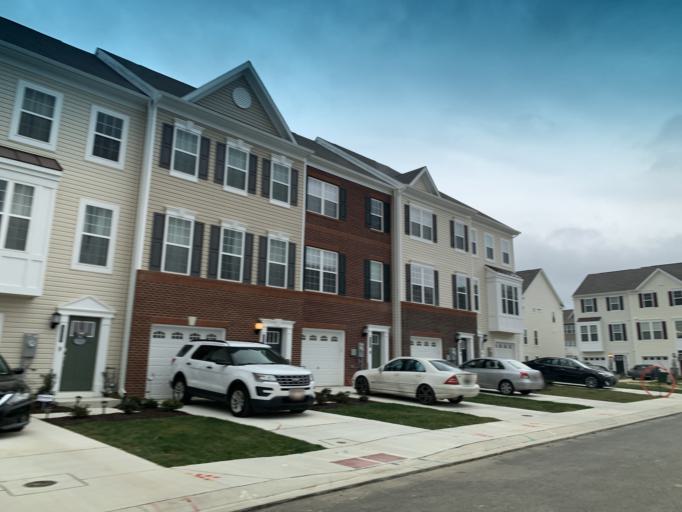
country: US
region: Maryland
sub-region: Harford County
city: Perryman
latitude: 39.4936
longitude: -76.2034
